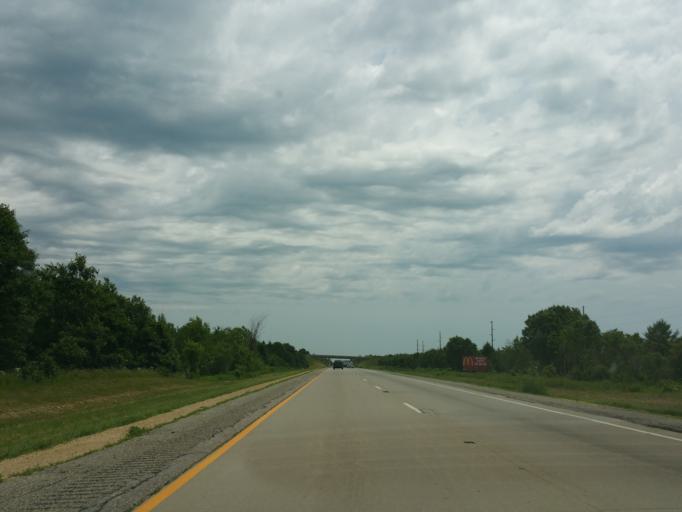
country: US
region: Wisconsin
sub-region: Columbia County
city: Wisconsin Dells
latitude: 43.7047
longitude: -89.8731
